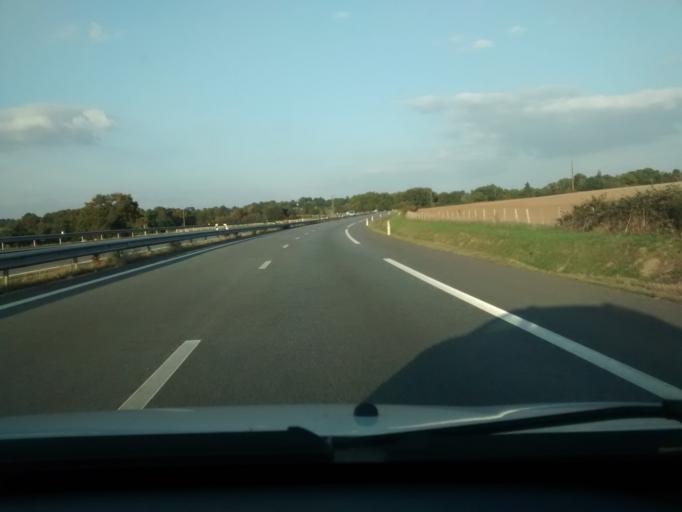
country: FR
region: Brittany
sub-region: Departement d'Ille-et-Vilaine
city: La Dominelais
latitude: 47.7724
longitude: -1.7069
